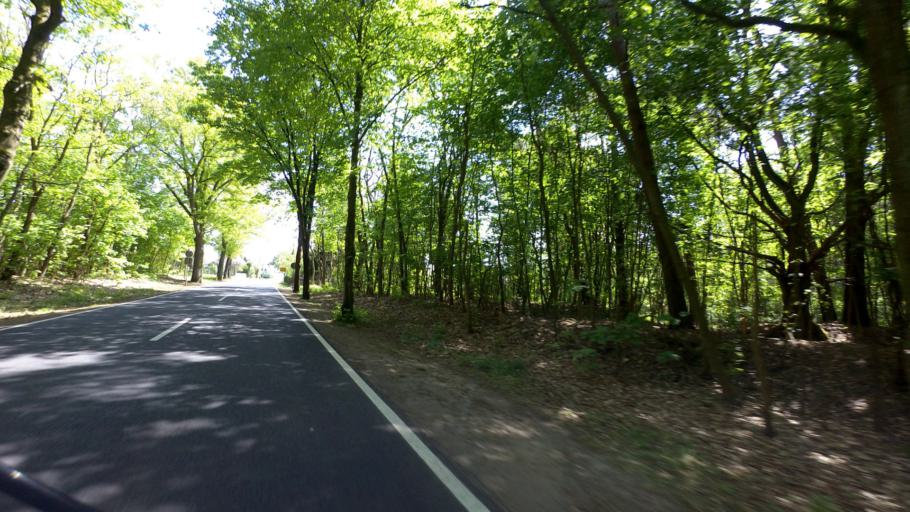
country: DE
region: Brandenburg
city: Munchehofe
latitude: 52.0884
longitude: 13.8646
